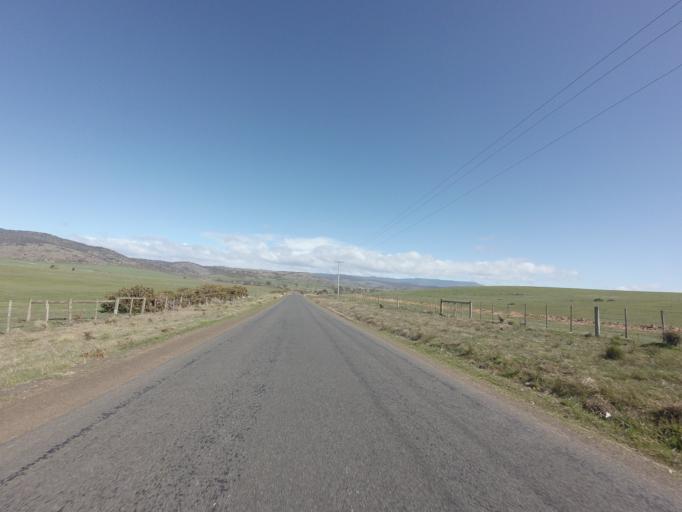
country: AU
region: Tasmania
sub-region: Northern Midlands
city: Evandale
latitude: -41.9018
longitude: 147.4012
